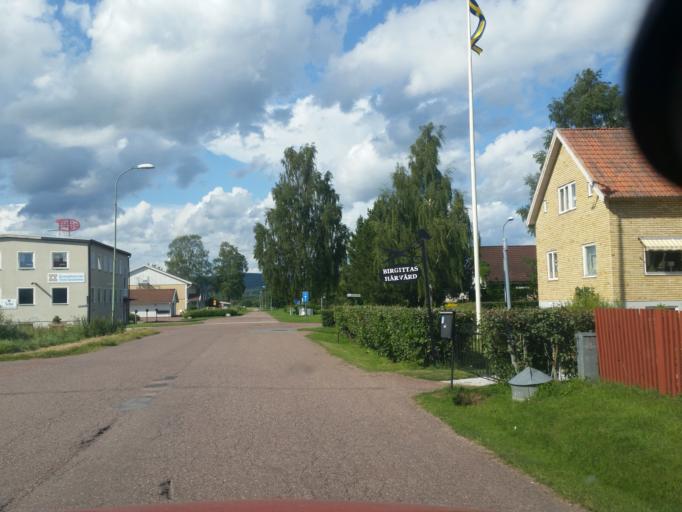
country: SE
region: Dalarna
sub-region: Leksand Municipality
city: Smedby
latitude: 60.6811
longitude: 15.0908
